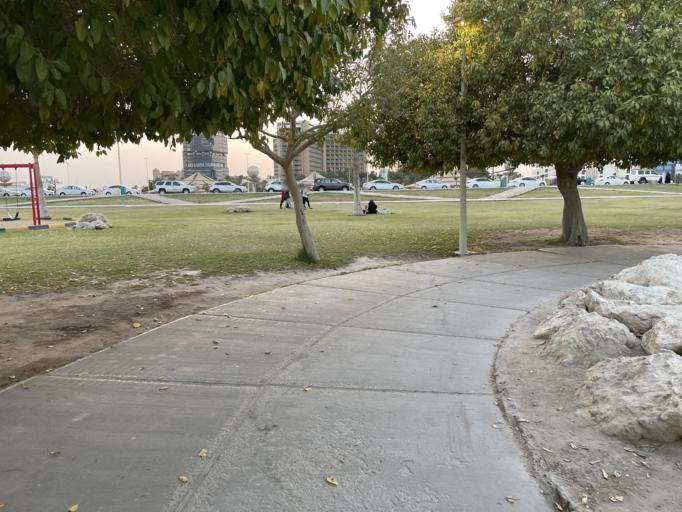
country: SA
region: Eastern Province
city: Khobar
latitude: 26.3020
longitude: 50.2278
